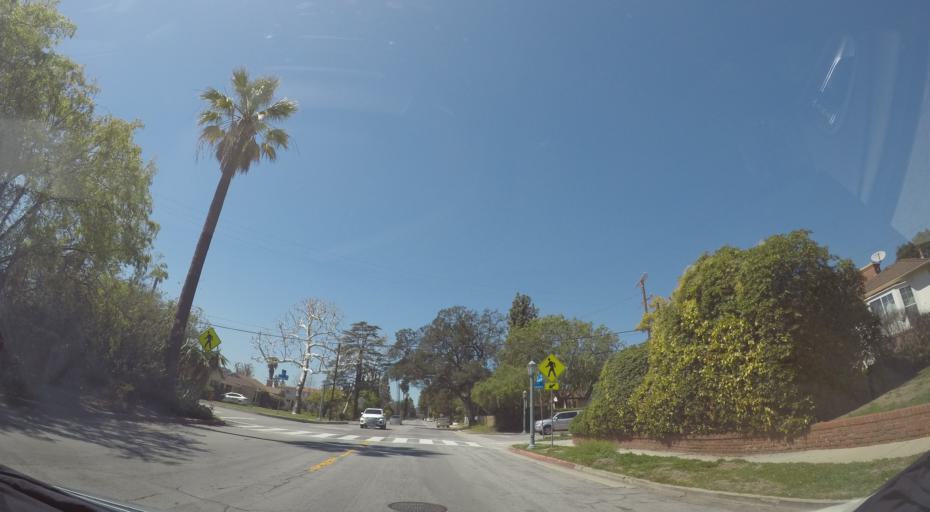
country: US
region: California
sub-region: Los Angeles County
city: Altadena
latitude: 34.1786
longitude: -118.1156
